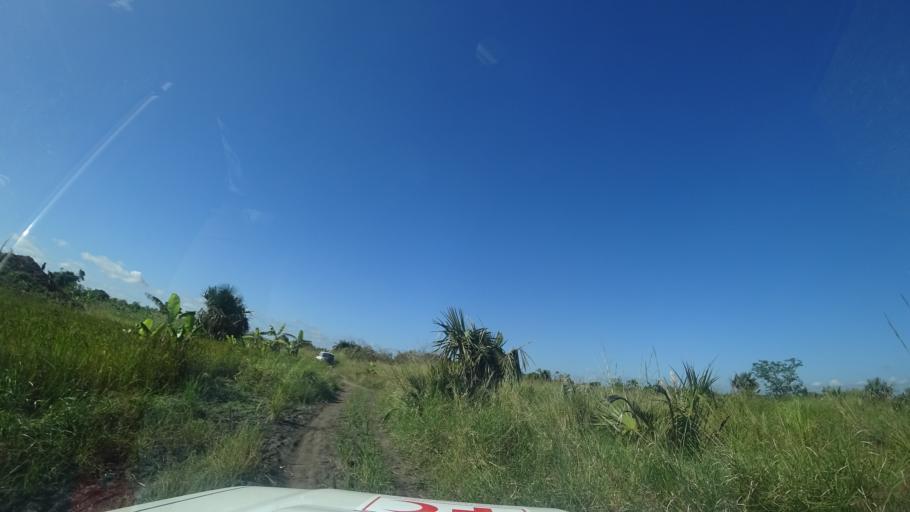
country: MZ
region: Sofala
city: Dondo
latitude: -19.3928
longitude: 34.5919
